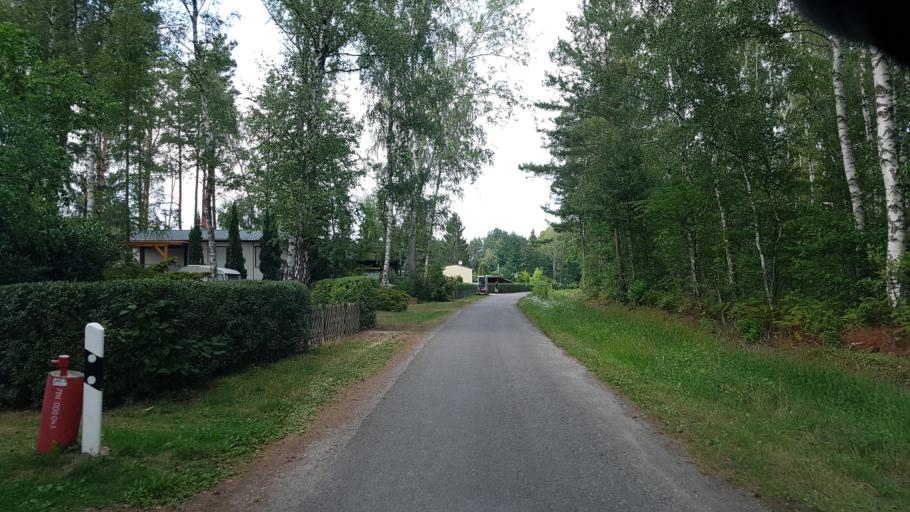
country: DE
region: Brandenburg
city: Plessa
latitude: 51.5138
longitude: 13.6693
